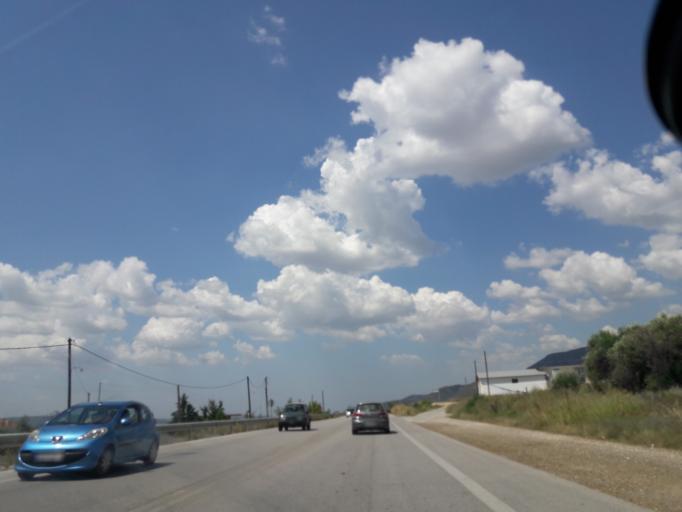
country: GR
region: Central Macedonia
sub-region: Nomos Chalkidikis
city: Galatista
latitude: 40.4633
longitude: 23.2706
